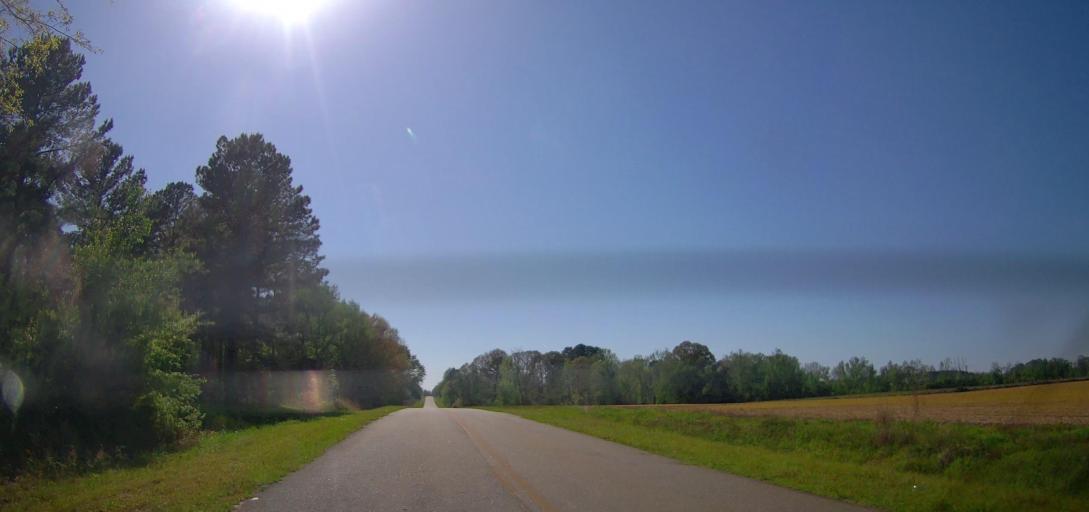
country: US
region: Georgia
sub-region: Pulaski County
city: Hawkinsville
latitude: 32.2477
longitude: -83.4781
